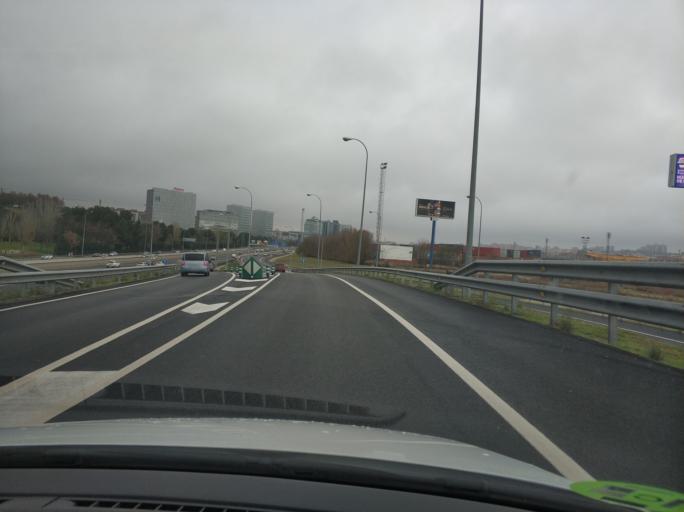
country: ES
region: Madrid
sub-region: Provincia de Madrid
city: Usera
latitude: 40.3848
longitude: -3.6818
